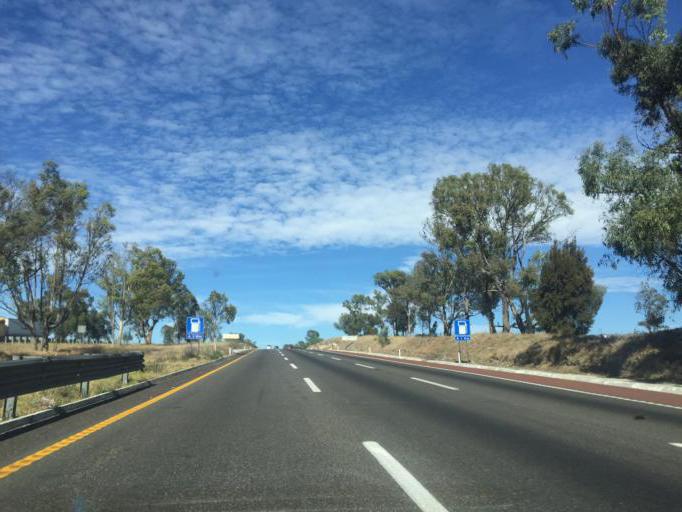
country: MX
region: Queretaro
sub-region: San Juan del Rio
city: El Cazadero
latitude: 20.2888
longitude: -99.9158
